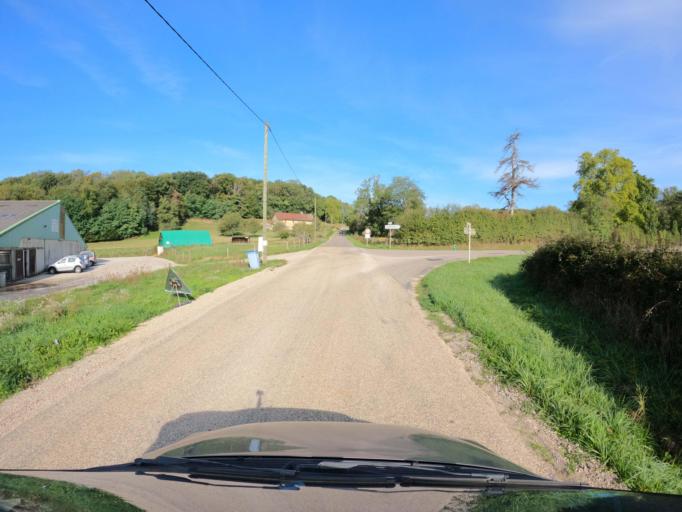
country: FR
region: Franche-Comte
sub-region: Departement du Jura
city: Montmorot
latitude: 46.7070
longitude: 5.5274
